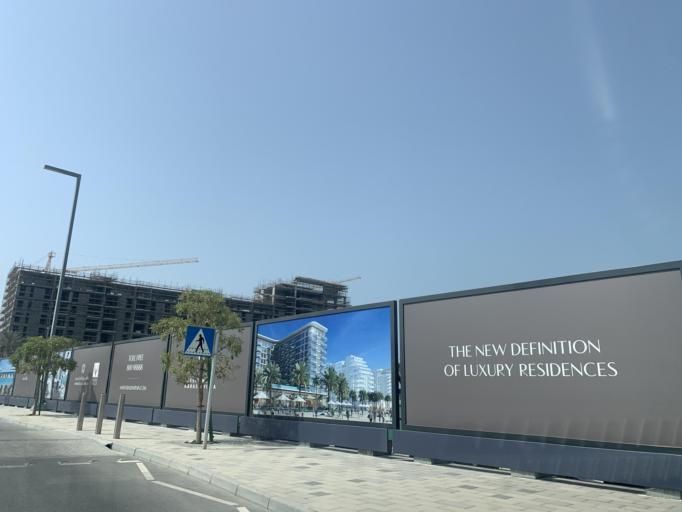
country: BH
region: Muharraq
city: Al Muharraq
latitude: 26.3059
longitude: 50.6461
